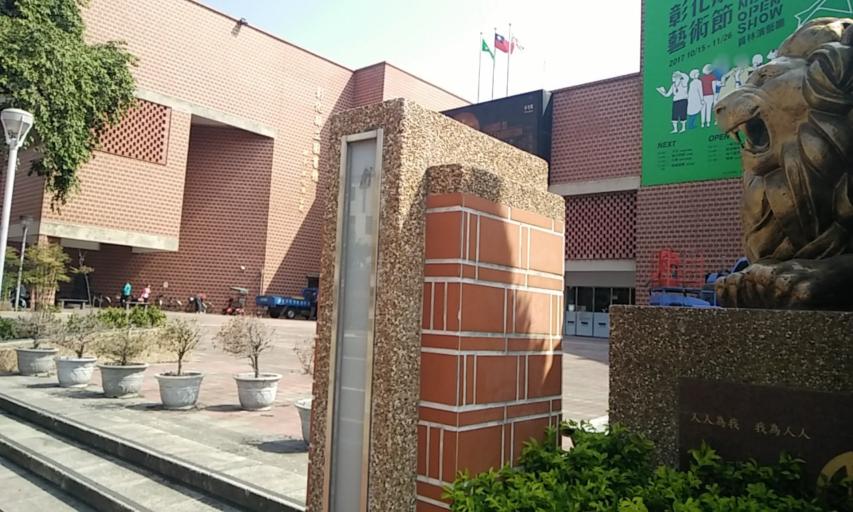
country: TW
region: Taiwan
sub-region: Changhua
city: Chang-hua
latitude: 24.0785
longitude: 120.5449
